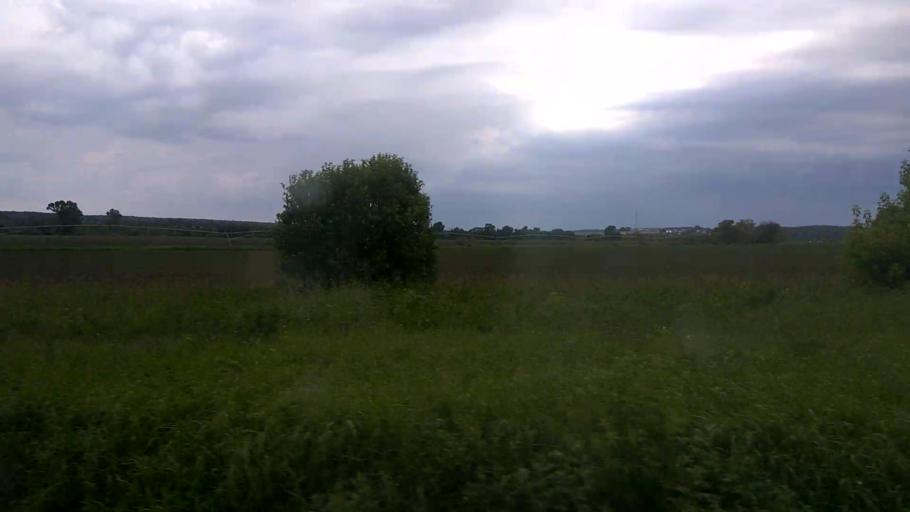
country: RU
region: Moskovskaya
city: Ozery
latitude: 54.8396
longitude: 38.5775
